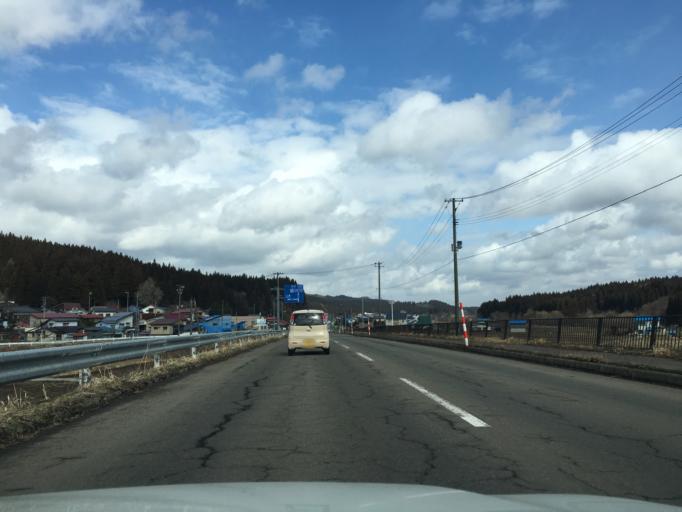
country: JP
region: Akita
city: Takanosu
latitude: 40.0306
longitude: 140.2744
